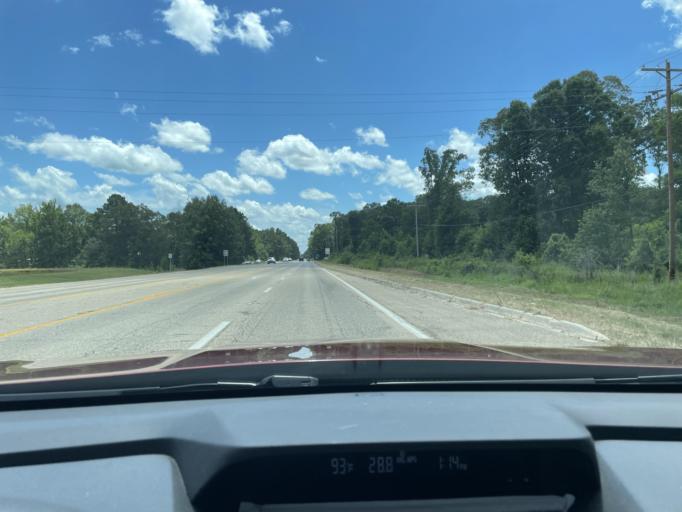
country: US
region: Arkansas
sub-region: Drew County
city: Monticello
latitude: 33.6600
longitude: -91.8032
